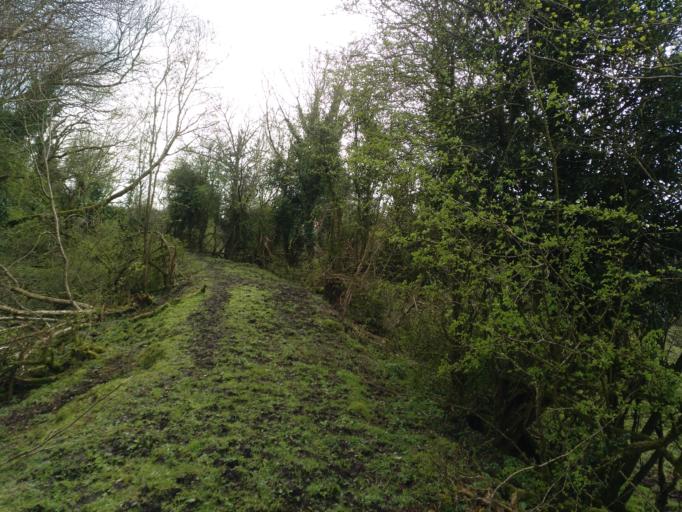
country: IE
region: Ulster
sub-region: County Monaghan
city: Clones
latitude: 54.2014
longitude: -7.1372
